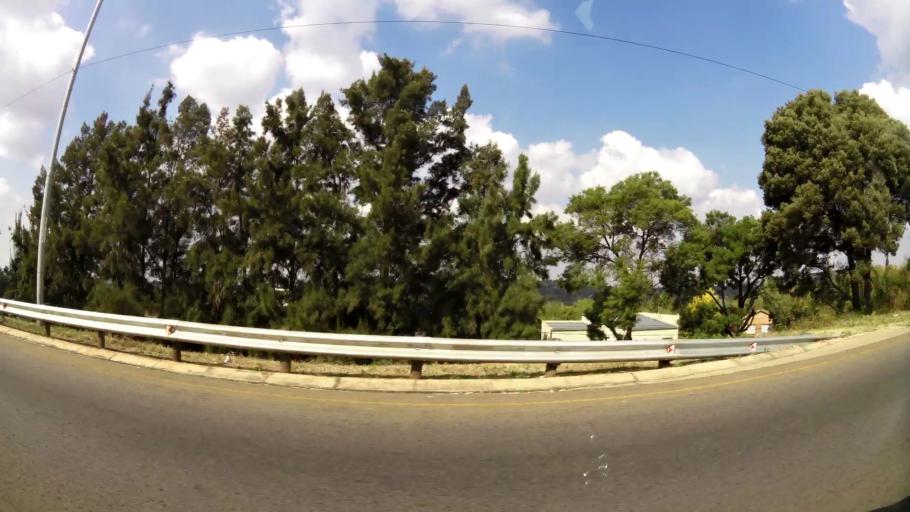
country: ZA
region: Gauteng
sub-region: City of Tshwane Metropolitan Municipality
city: Centurion
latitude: -25.8165
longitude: 28.2756
